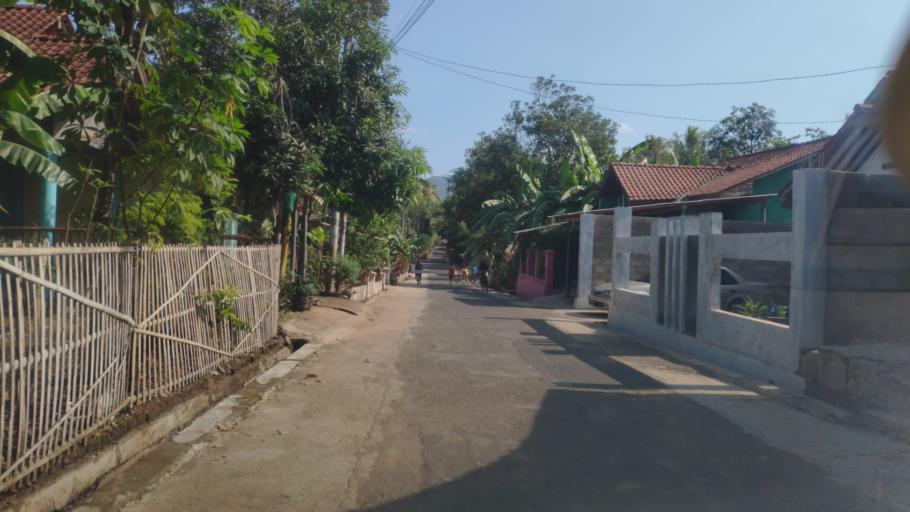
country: ID
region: Central Java
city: Purbalingga
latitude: -7.4722
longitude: 109.4482
